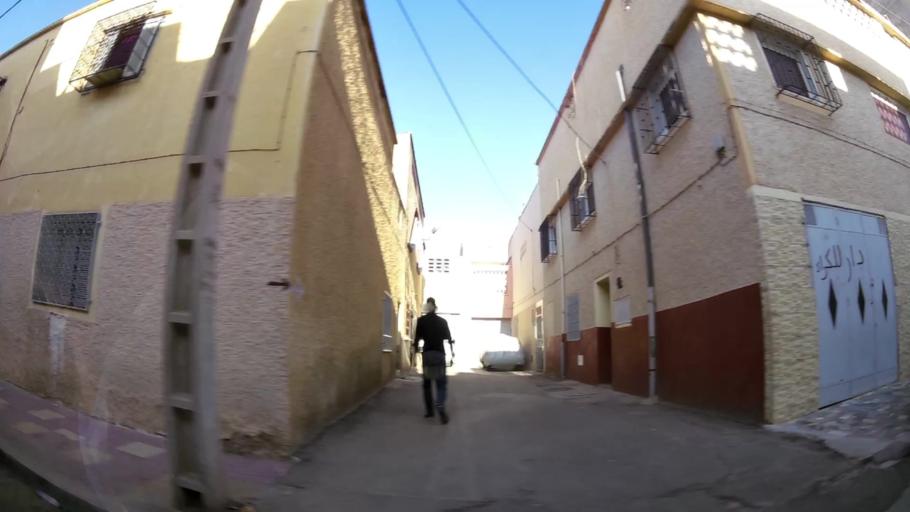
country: MA
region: Oriental
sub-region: Oujda-Angad
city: Oujda
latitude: 34.6947
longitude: -1.9126
